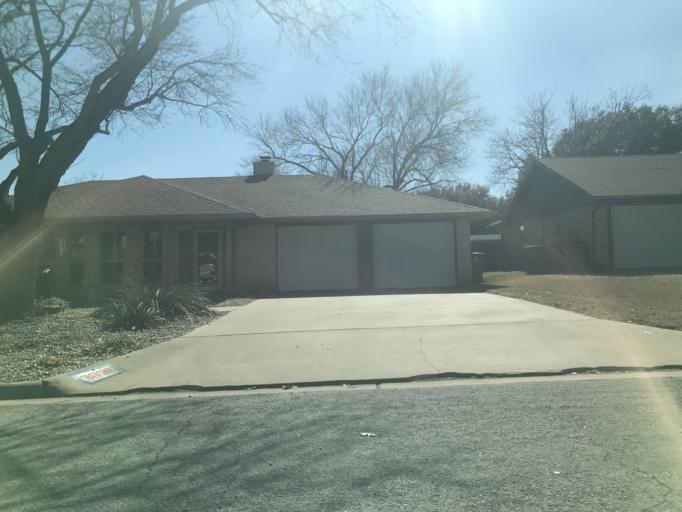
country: US
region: Texas
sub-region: Tom Green County
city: San Angelo
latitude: 31.4289
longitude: -100.4914
